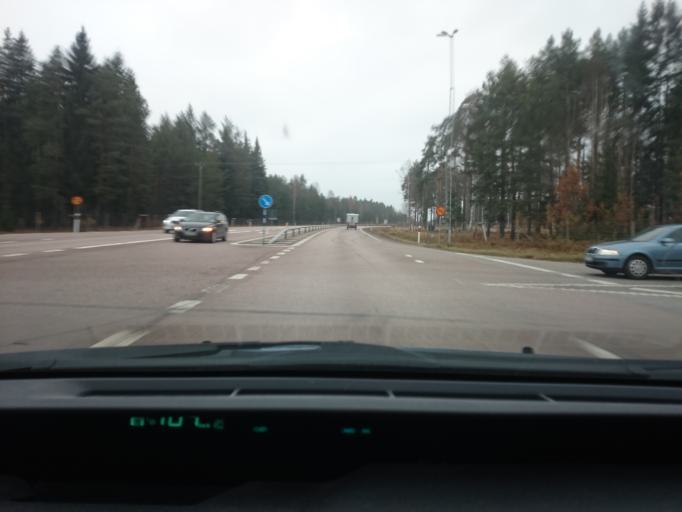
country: SE
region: Dalarna
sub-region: Avesta Kommun
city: Avesta
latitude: 60.1063
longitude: 16.3000
